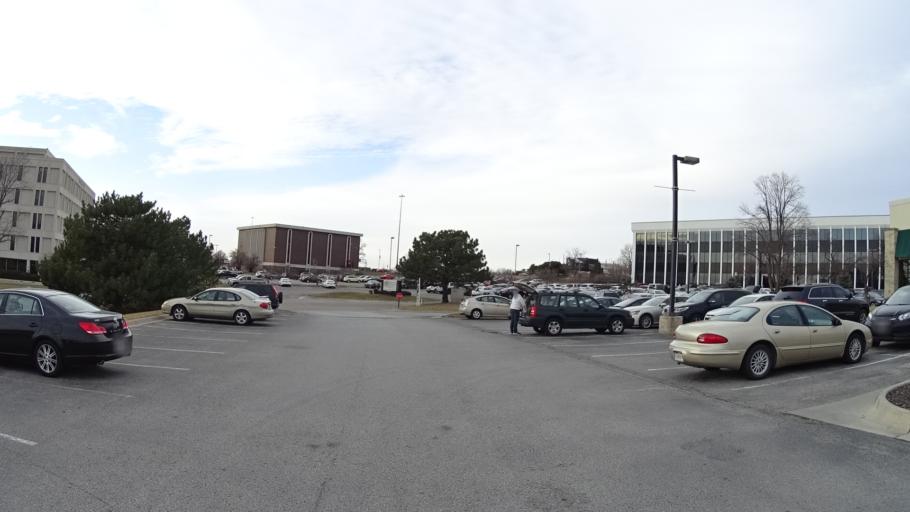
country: US
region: Nebraska
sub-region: Douglas County
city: Ralston
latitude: 41.2616
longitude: -96.0691
